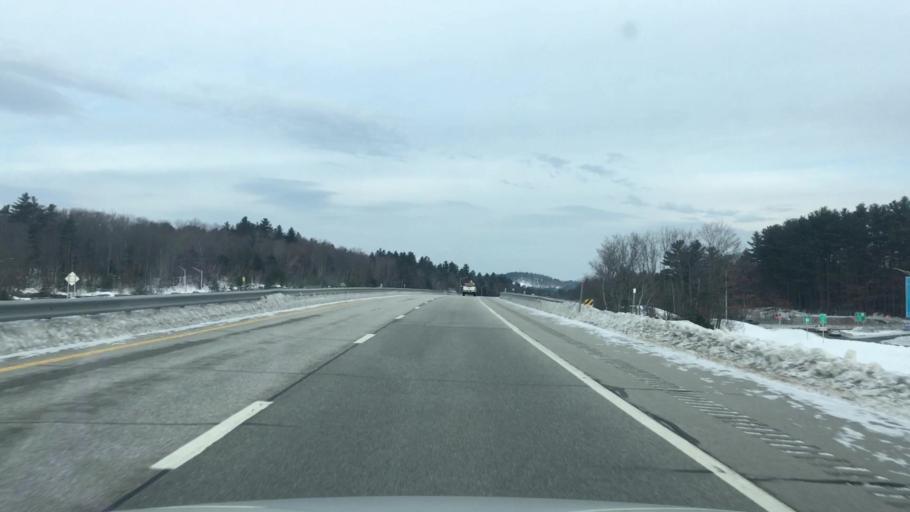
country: US
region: New Hampshire
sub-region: Merrimack County
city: New London
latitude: 43.4210
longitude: -72.0361
